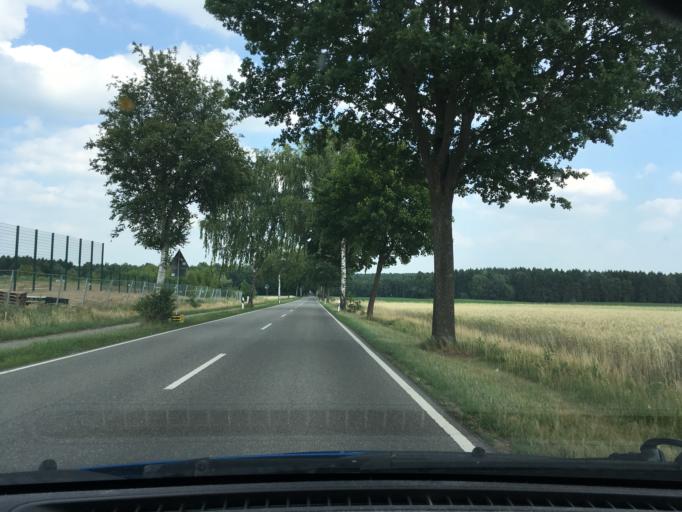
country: DE
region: Lower Saxony
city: Buchholz in der Nordheide
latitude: 53.3318
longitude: 9.9001
